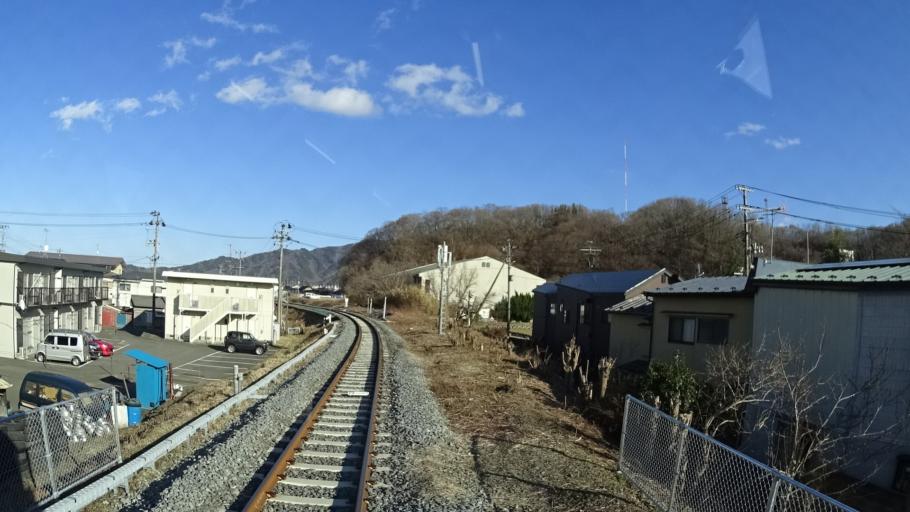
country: JP
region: Iwate
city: Miyako
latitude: 39.6375
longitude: 141.9563
